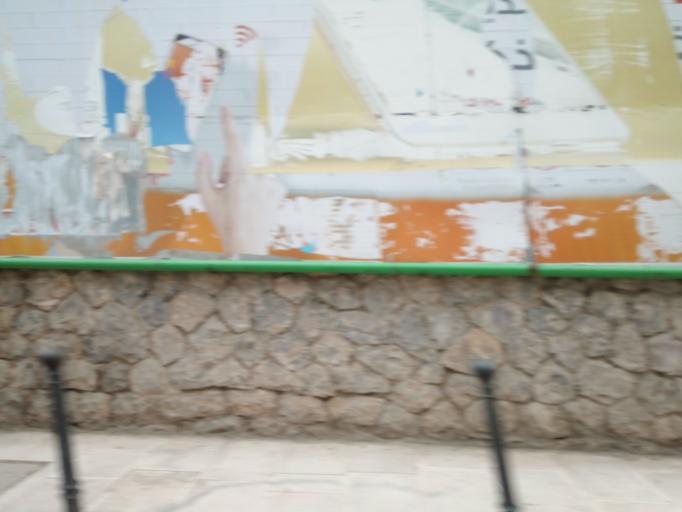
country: DZ
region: Constantine
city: Constantine
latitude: 36.3603
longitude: 6.6075
